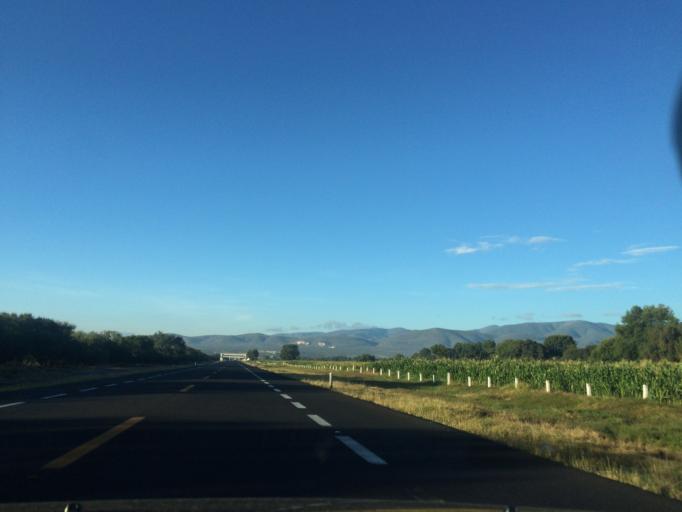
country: MX
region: Puebla
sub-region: Santiago Miahuatlan
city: San Jose Monte Chiquito
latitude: 18.5150
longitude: -97.4544
